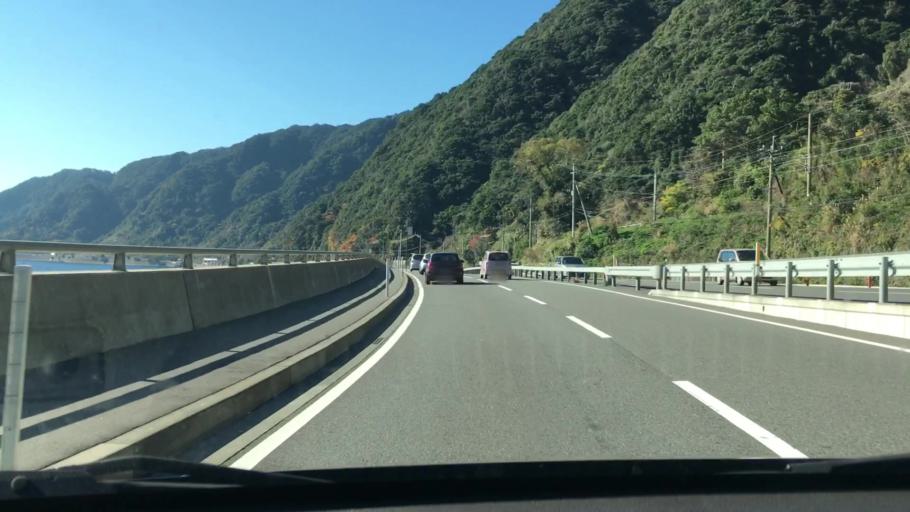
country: JP
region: Kagoshima
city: Kajiki
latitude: 31.6556
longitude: 130.6114
